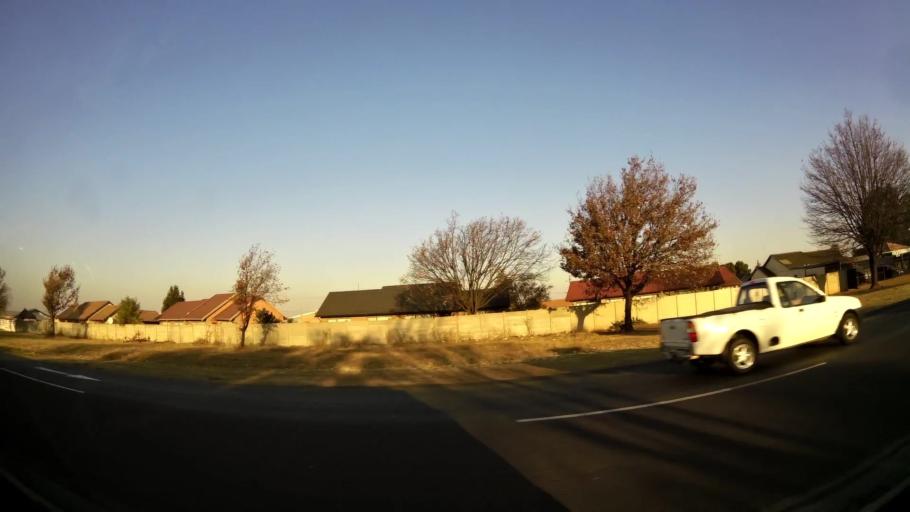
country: ZA
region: Gauteng
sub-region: West Rand District Municipality
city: Randfontein
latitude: -26.2089
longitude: 27.6575
